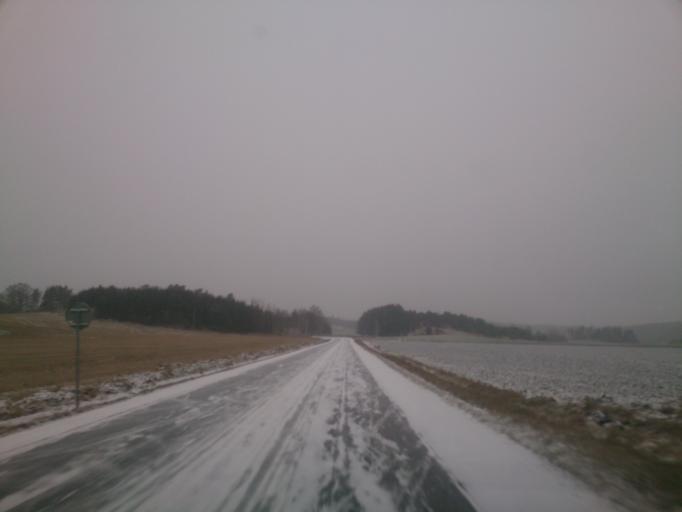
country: SE
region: OEstergoetland
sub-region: Norrkopings Kommun
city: Norrkoping
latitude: 58.4919
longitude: 16.1325
